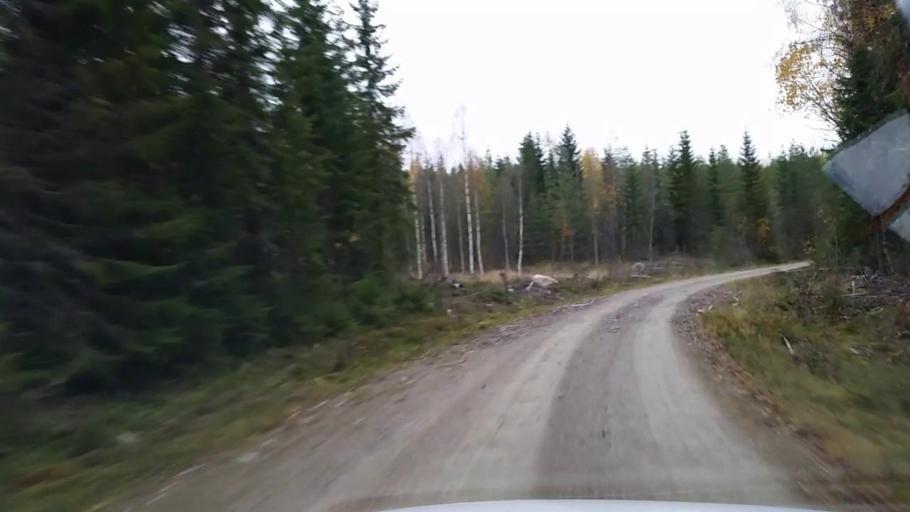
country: SE
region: Vaesternorrland
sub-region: Ange Kommun
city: Ange
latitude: 62.2690
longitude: 15.3657
